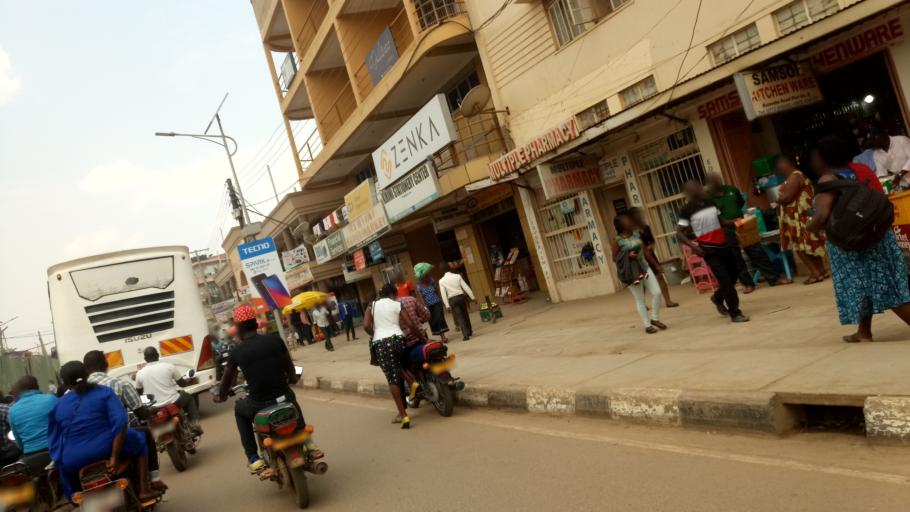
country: UG
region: Western Region
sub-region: Mbarara District
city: Mbarara
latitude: -0.6074
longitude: 30.6622
